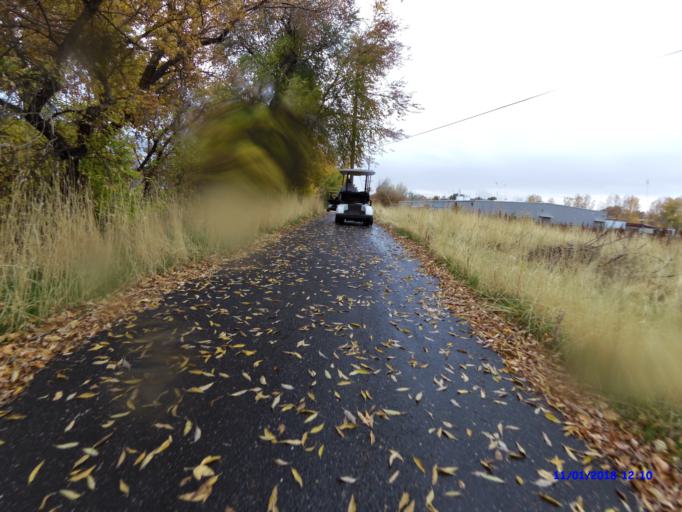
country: US
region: Utah
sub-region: Weber County
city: Ogden
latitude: 41.2262
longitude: -111.9874
